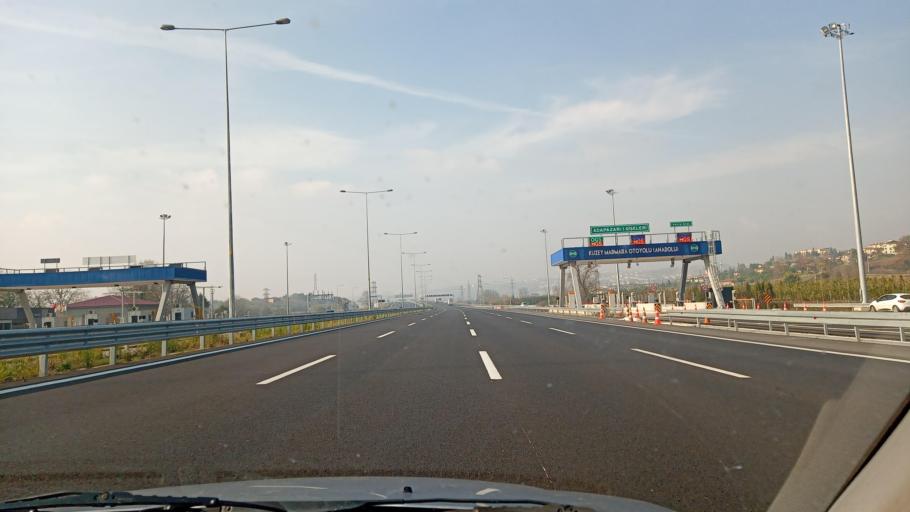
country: TR
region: Sakarya
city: Kazimpasa
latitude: 40.8428
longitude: 30.3437
